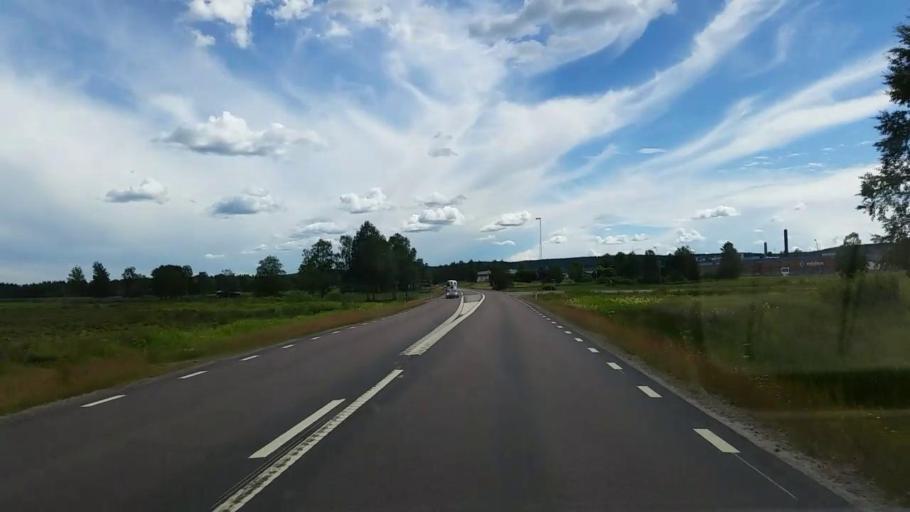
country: SE
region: Gaevleborg
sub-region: Ovanakers Kommun
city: Edsbyn
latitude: 61.3781
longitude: 15.8376
